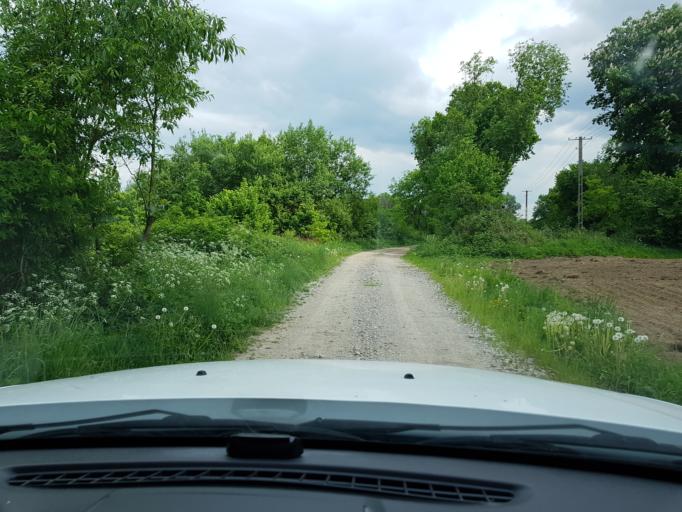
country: PL
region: West Pomeranian Voivodeship
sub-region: Powiat drawski
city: Drawsko Pomorskie
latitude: 53.5481
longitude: 15.7354
